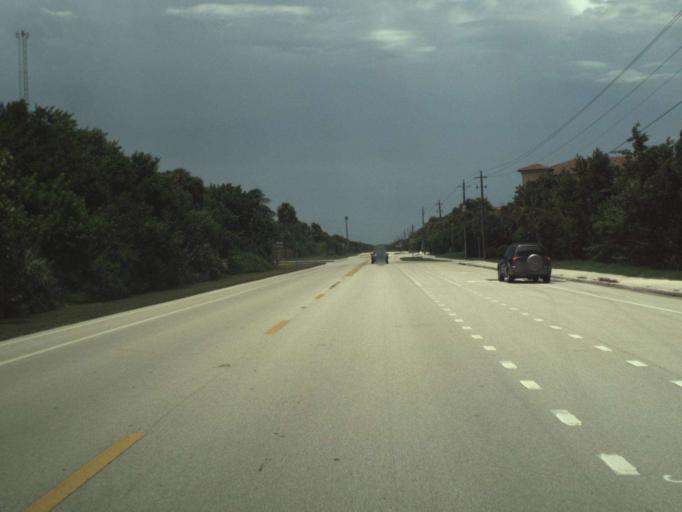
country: US
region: Florida
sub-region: Saint Lucie County
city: Hutchinson Island South
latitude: 27.3266
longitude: -80.2306
